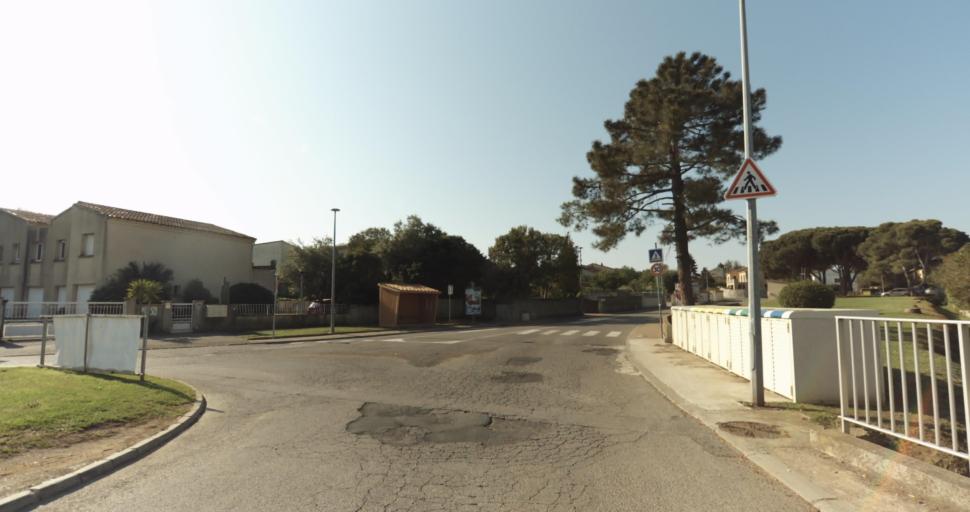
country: FR
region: Corsica
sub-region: Departement de la Haute-Corse
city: Biguglia
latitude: 42.6376
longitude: 9.4331
